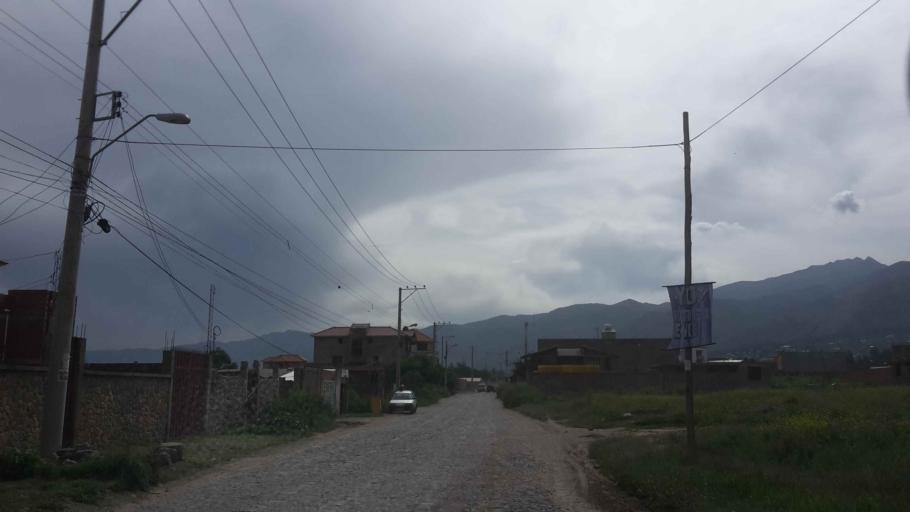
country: BO
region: Cochabamba
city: Cochabamba
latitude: -17.3363
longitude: -66.2588
